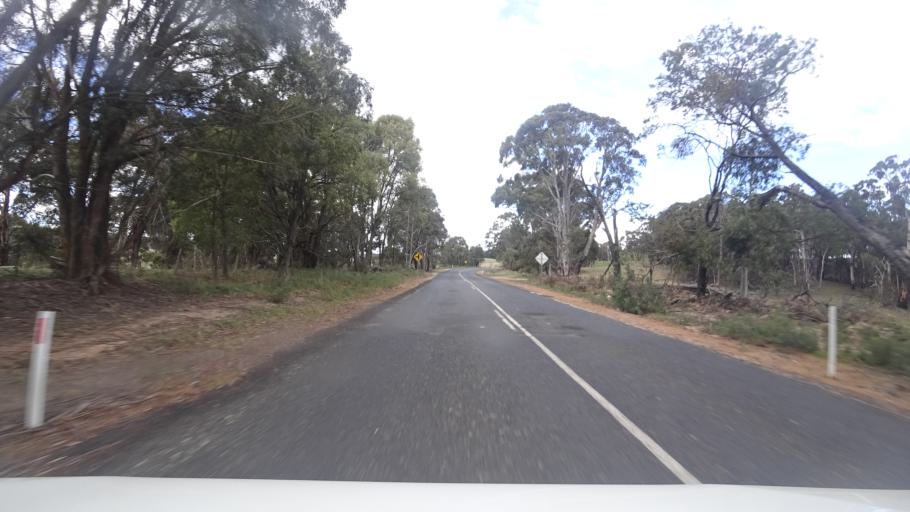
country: AU
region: New South Wales
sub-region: Oberon
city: Oberon
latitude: -33.6524
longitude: 149.8963
